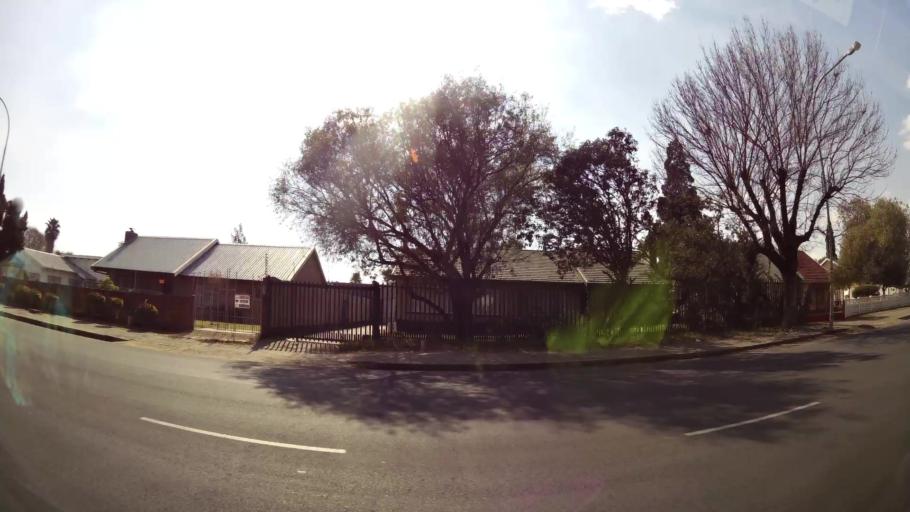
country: ZA
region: Gauteng
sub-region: City of Johannesburg Metropolitan Municipality
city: Modderfontein
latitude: -26.0898
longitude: 28.2235
